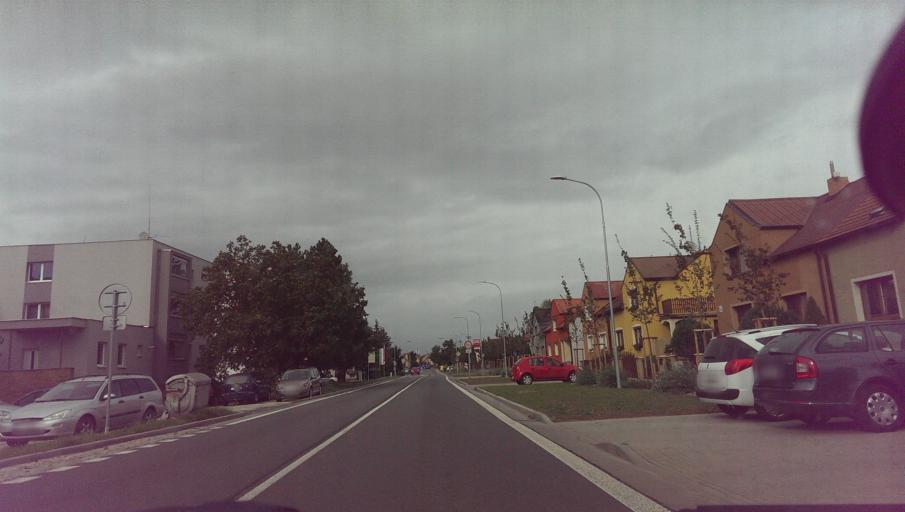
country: CZ
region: South Moravian
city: Veseli nad Moravou
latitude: 48.9625
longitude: 17.3927
